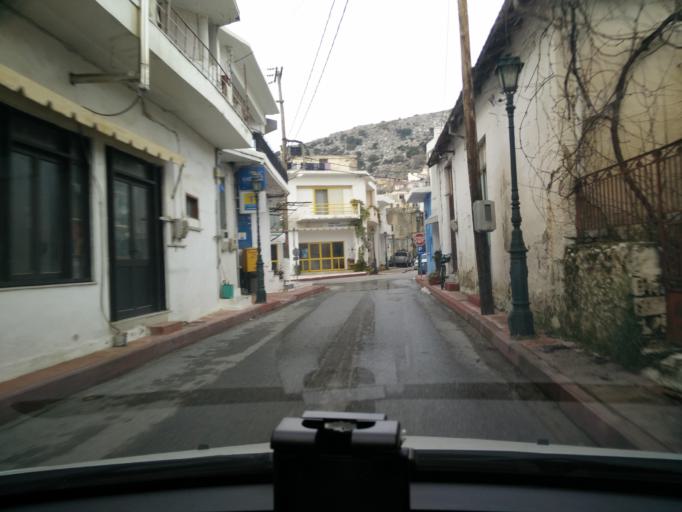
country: GR
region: Crete
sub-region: Nomos Irakleiou
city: Malia
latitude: 35.1981
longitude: 25.4888
